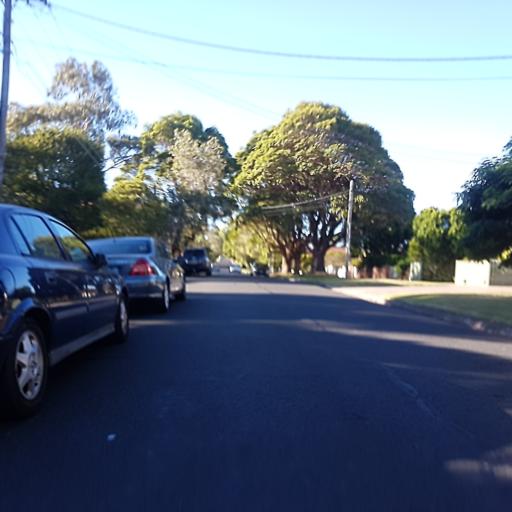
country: AU
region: New South Wales
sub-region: Willoughby
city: Castle Cove
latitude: -33.7942
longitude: 151.2047
